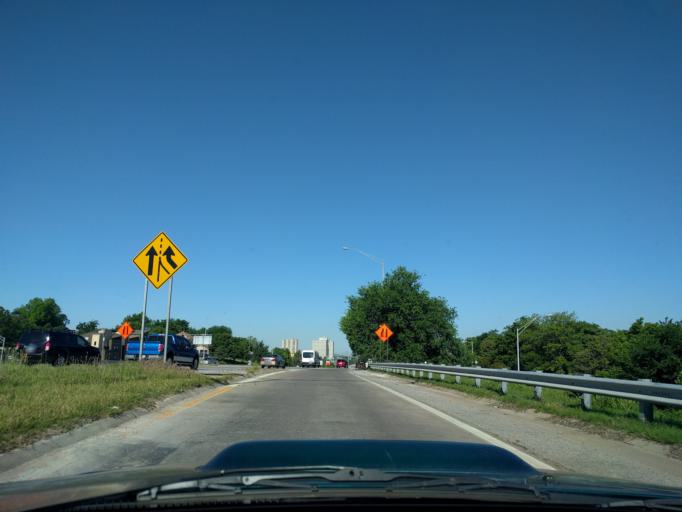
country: US
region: Oklahoma
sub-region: Tulsa County
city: Tulsa
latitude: 36.1431
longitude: -95.9698
